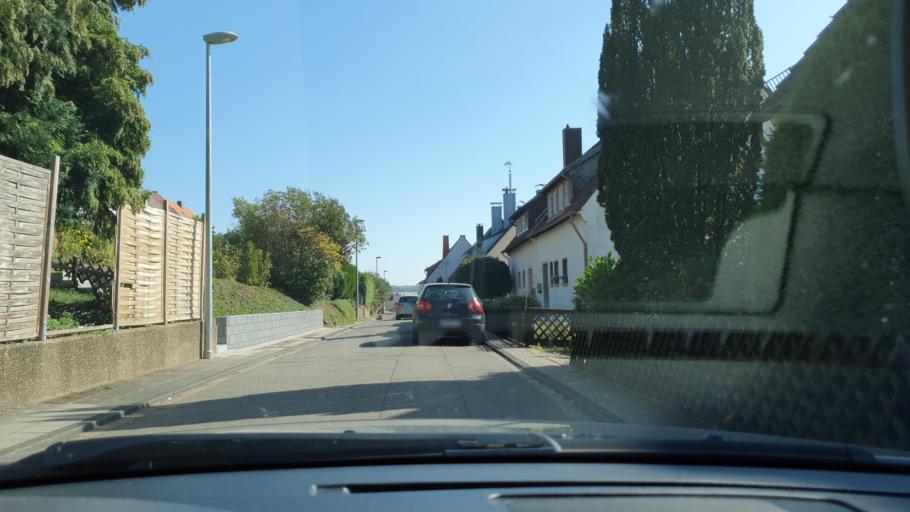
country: DE
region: Rheinland-Pfalz
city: Zweibrucken
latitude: 49.2581
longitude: 7.3415
